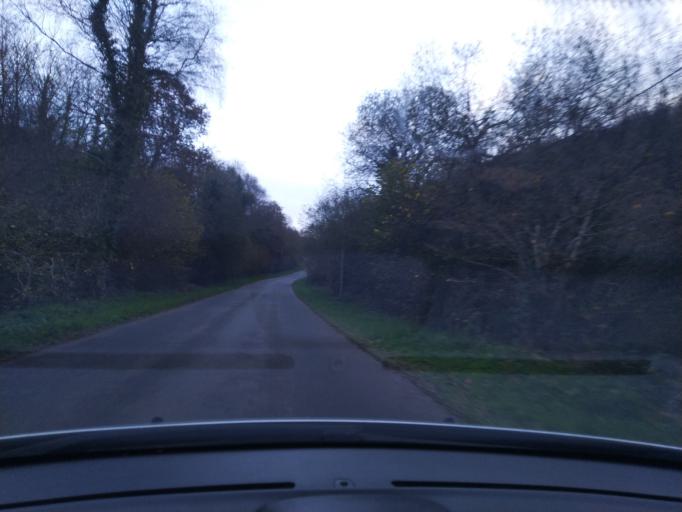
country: FR
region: Brittany
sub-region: Departement du Finistere
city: Guerlesquin
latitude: 48.5347
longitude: -3.6130
